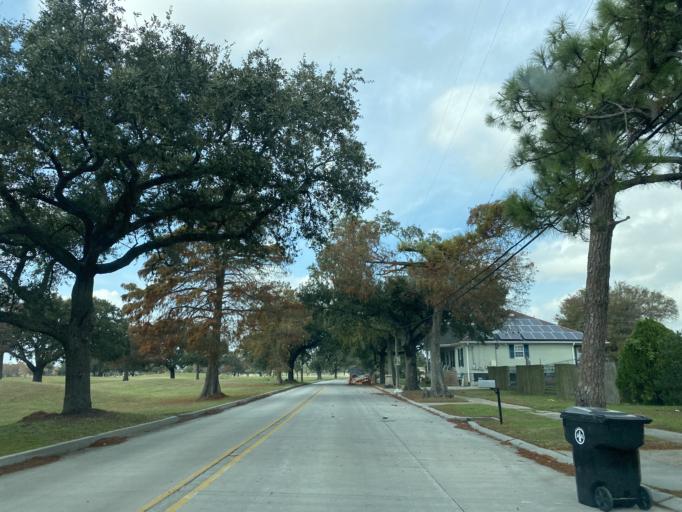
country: US
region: Louisiana
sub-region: Saint Bernard Parish
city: Arabi
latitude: 30.0221
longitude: -90.0374
